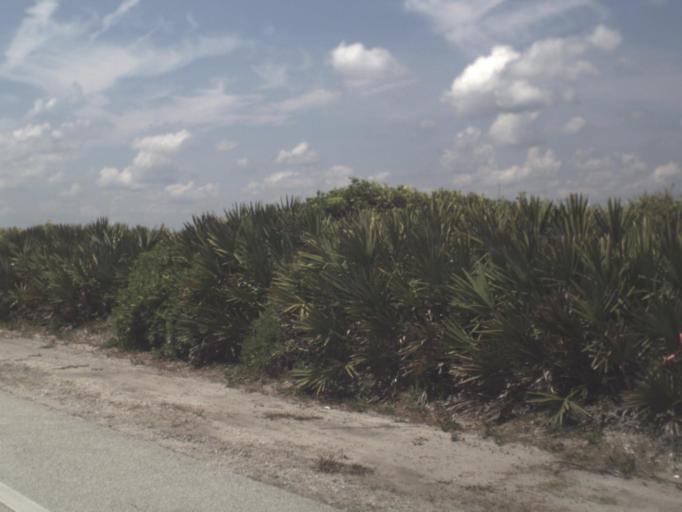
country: US
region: Florida
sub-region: Saint Johns County
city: Villano Beach
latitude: 30.0023
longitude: -81.3182
